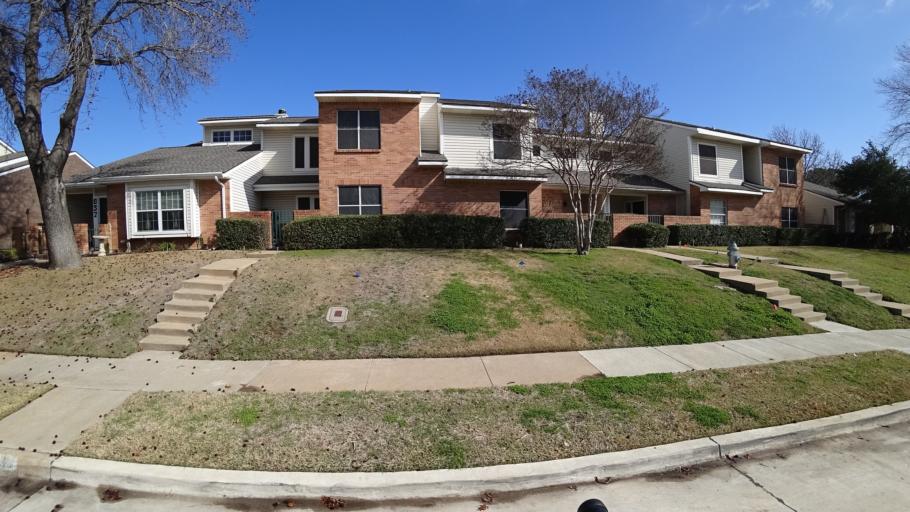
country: US
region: Texas
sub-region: Denton County
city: Lewisville
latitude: 33.0345
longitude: -97.0040
